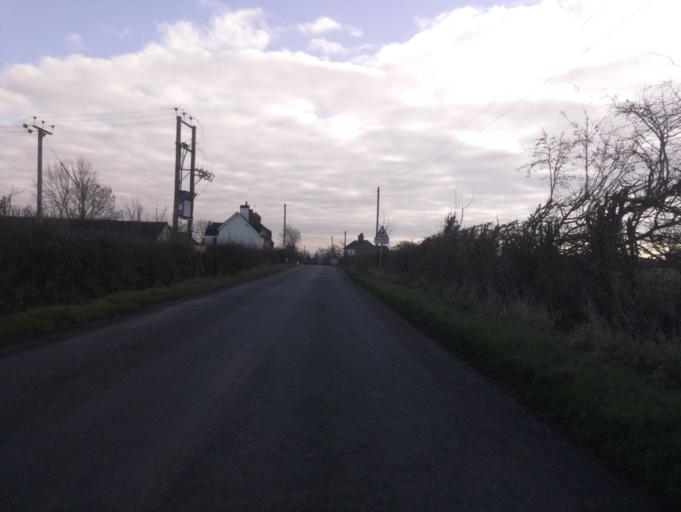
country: GB
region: England
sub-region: Staffordshire
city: Barton under Needwood
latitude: 52.7986
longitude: -1.7143
